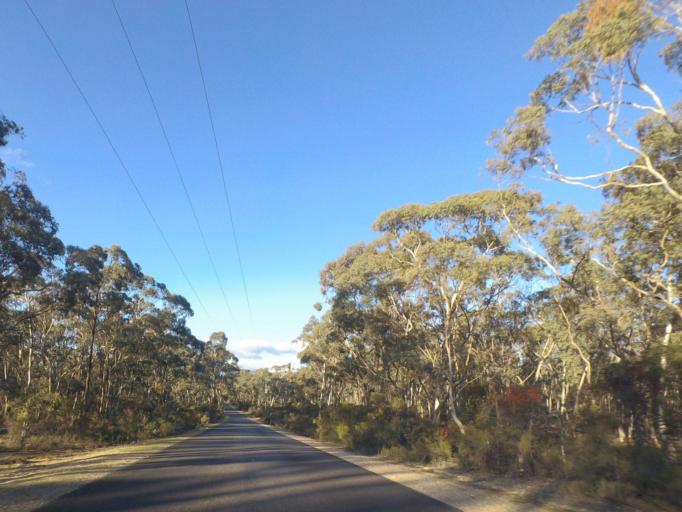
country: AU
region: Victoria
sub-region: Mount Alexander
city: Castlemaine
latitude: -37.1429
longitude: 144.1933
